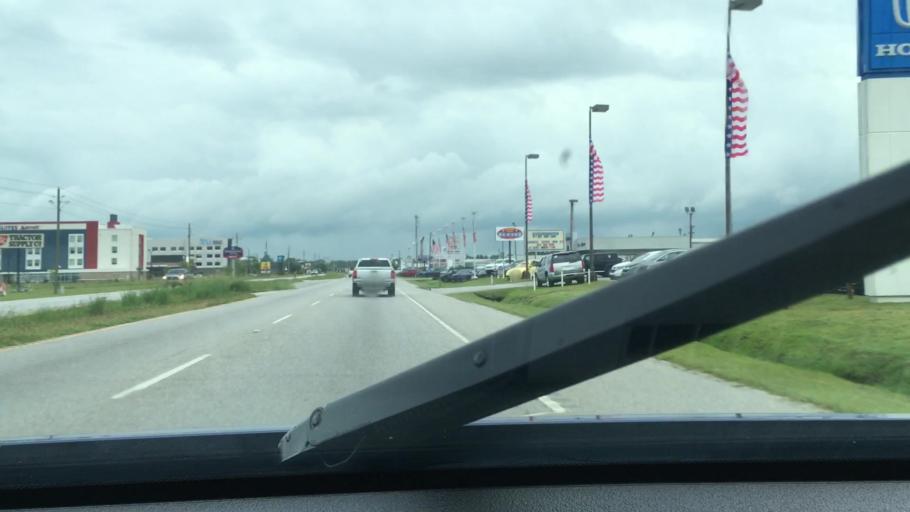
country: US
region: South Carolina
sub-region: Sumter County
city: Cherryvale
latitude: 33.9628
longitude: -80.4025
